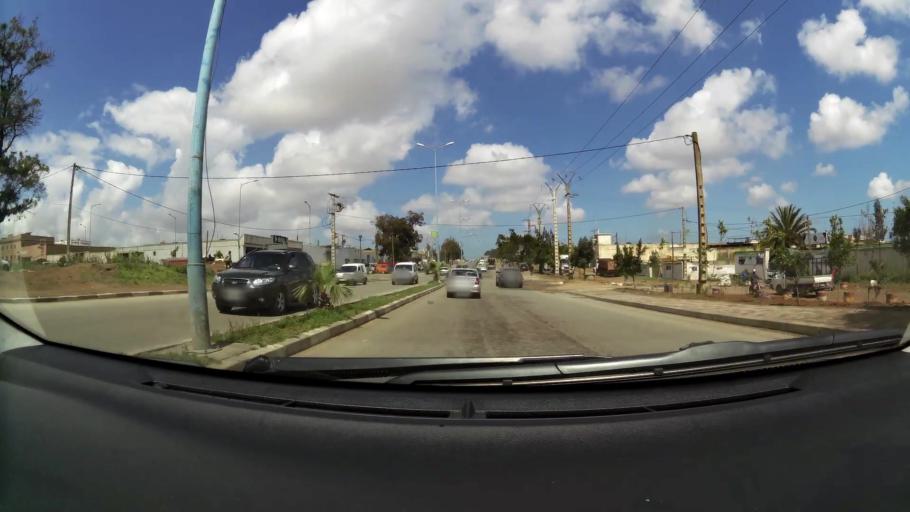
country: MA
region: Grand Casablanca
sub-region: Casablanca
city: Casablanca
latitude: 33.5300
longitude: -7.5679
